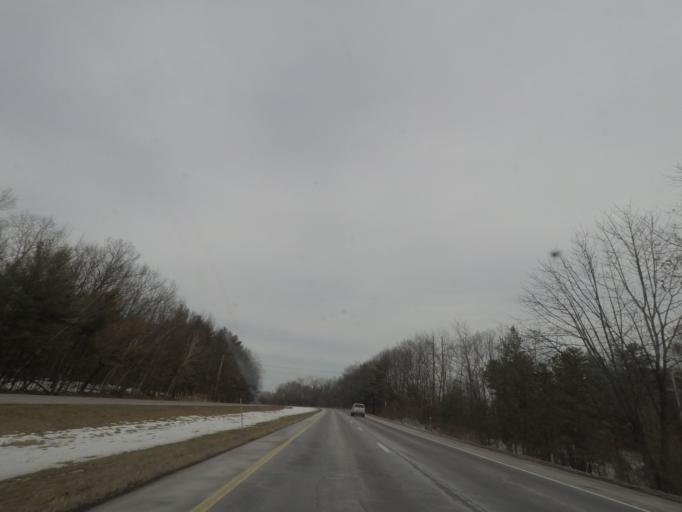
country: US
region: New York
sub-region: Albany County
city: Delmar
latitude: 42.6052
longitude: -73.8279
